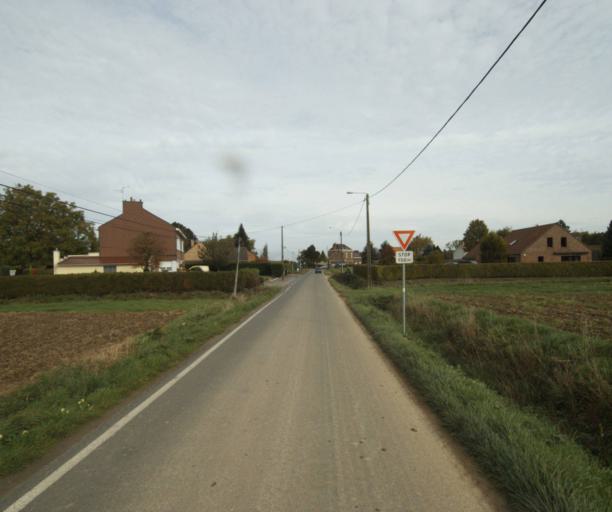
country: FR
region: Nord-Pas-de-Calais
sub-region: Departement du Nord
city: Fournes-en-Weppes
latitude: 50.6066
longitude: 2.8665
